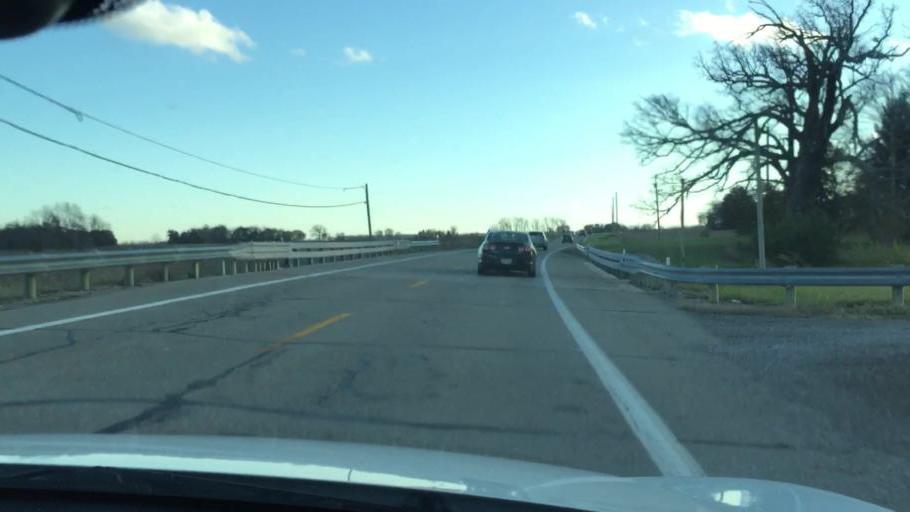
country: US
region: Ohio
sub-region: Champaign County
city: North Lewisburg
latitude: 40.1643
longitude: -83.5268
